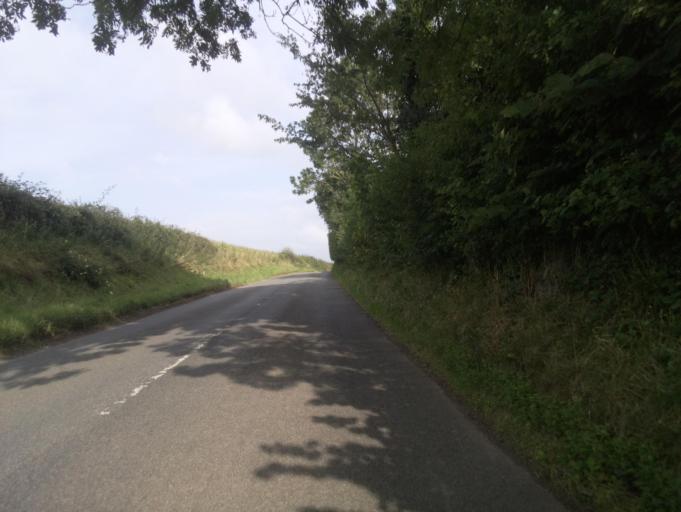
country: GB
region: England
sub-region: Bath and North East Somerset
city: East Harptree
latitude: 51.2929
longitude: -2.5964
